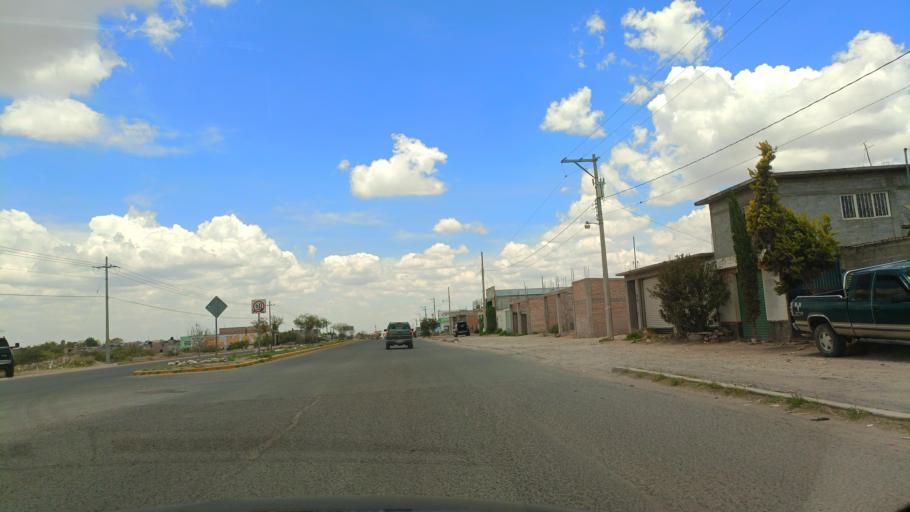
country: MX
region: Guanajuato
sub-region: San Luis de la Paz
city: San Luis de la Paz
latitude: 21.2899
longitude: -100.4974
